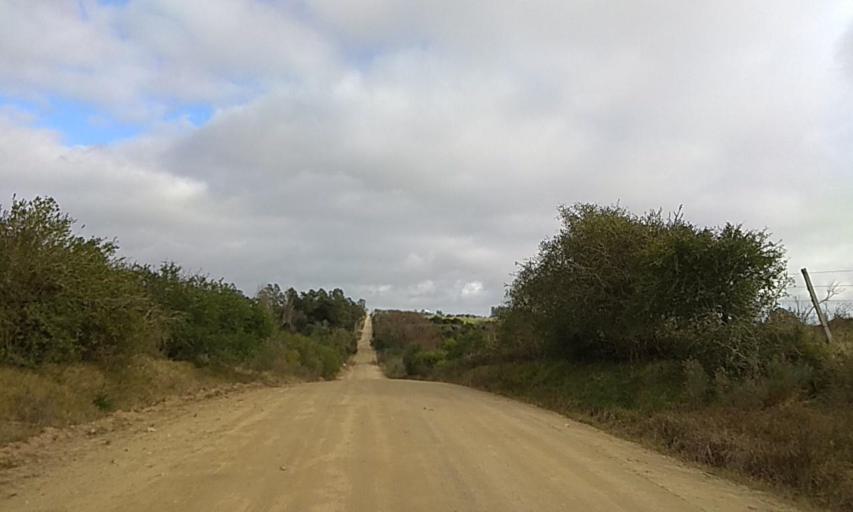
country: UY
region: Florida
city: Florida
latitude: -34.0596
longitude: -56.2131
